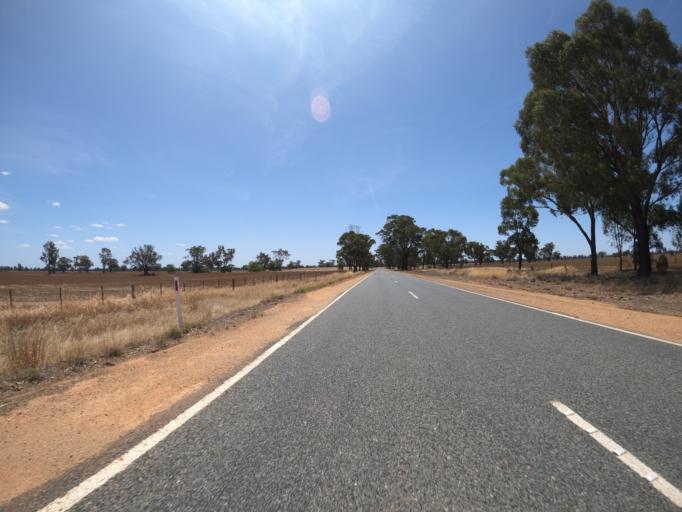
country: AU
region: Victoria
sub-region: Moira
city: Yarrawonga
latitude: -36.1961
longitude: 145.9670
